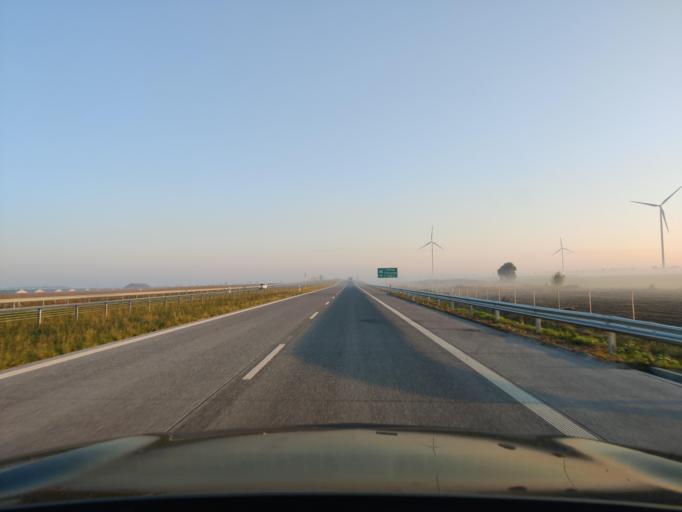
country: PL
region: Masovian Voivodeship
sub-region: Powiat mlawski
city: Wisniewo
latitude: 53.0449
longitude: 20.3592
